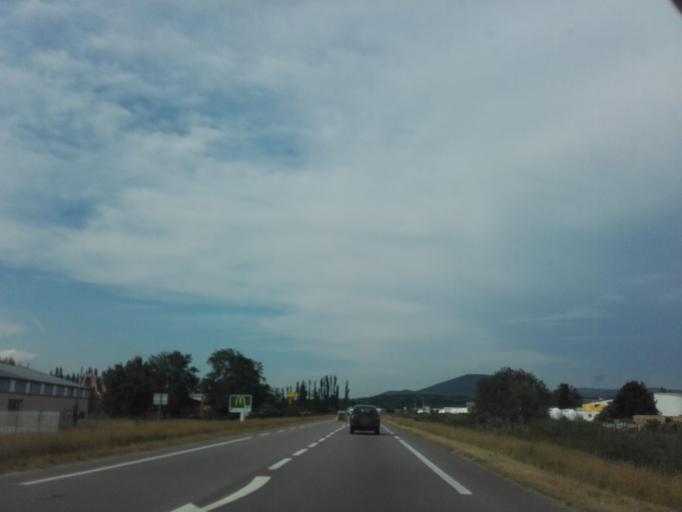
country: FR
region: Rhone-Alpes
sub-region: Departement de la Drome
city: Ancone
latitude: 44.5745
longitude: 4.7414
